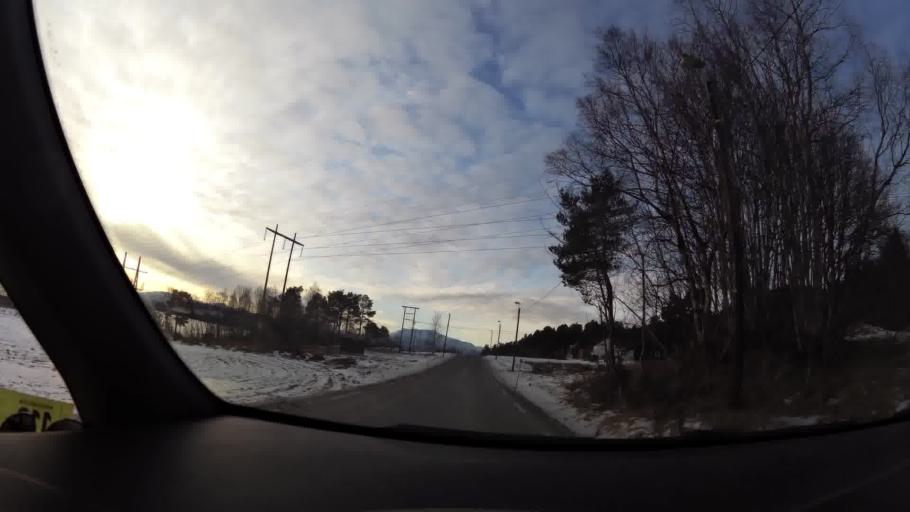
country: NO
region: More og Romsdal
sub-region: Kristiansund
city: Rensvik
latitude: 63.0829
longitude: 7.8848
